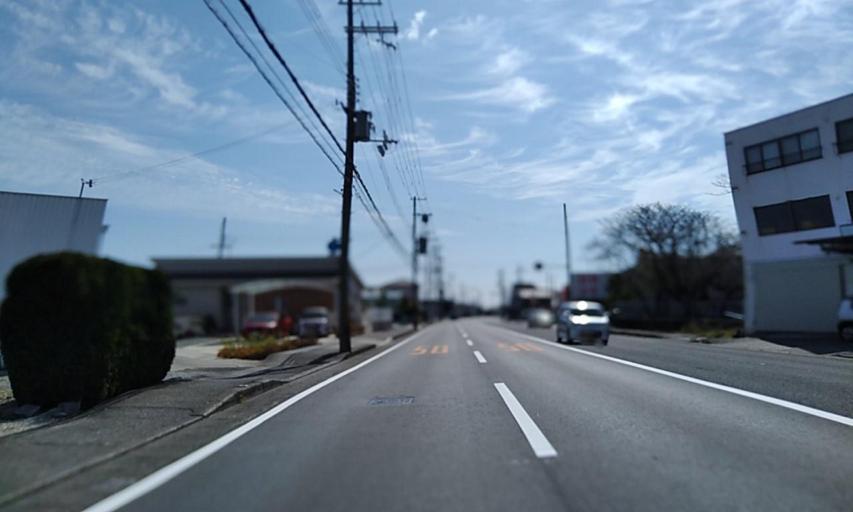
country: JP
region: Wakayama
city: Gobo
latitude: 33.8972
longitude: 135.1625
